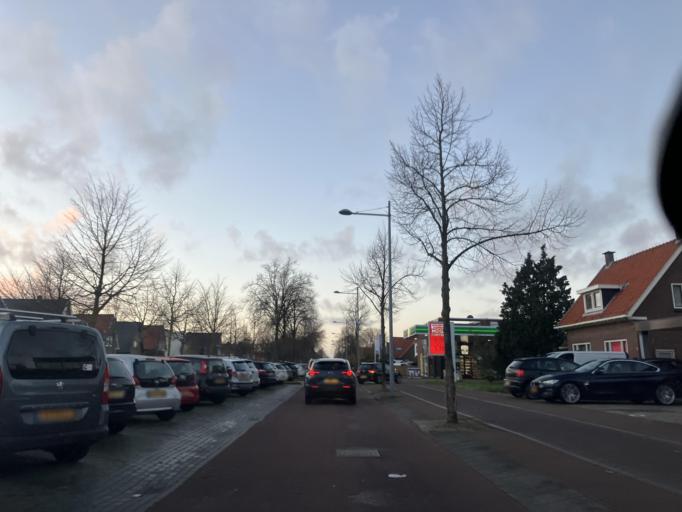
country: NL
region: South Holland
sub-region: Gemeente Kaag en Braassem
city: Oude Wetering
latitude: 52.2660
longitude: 4.6317
